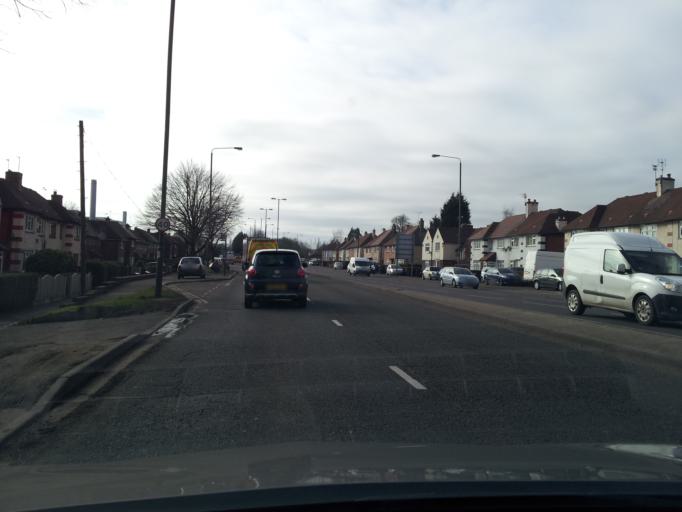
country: GB
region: England
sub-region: Derby
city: Derby
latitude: 52.9137
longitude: -1.5097
